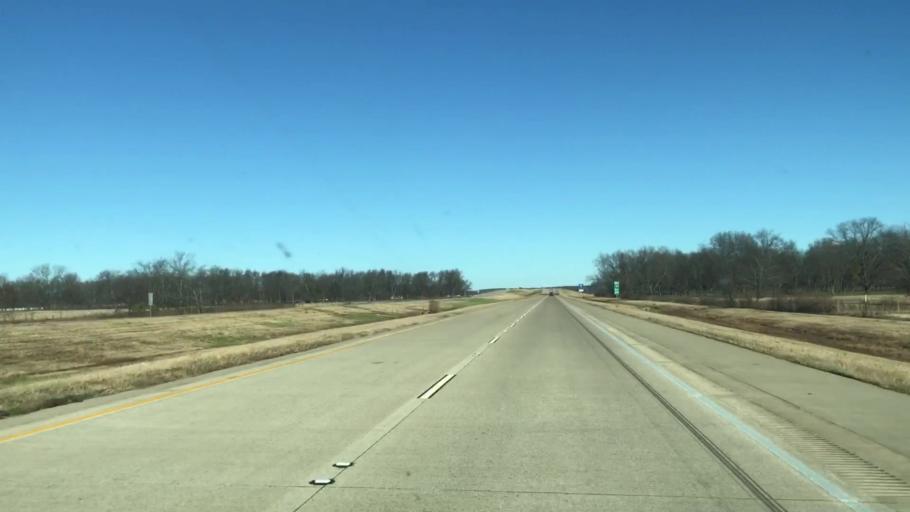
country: US
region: Louisiana
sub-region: Caddo Parish
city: Oil City
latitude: 32.7386
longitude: -93.8766
